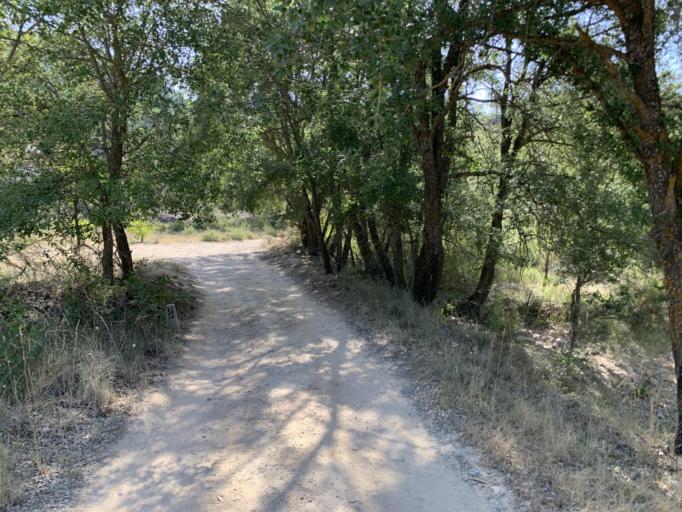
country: ES
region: Castille-La Mancha
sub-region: Provincia de Guadalajara
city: Ocentejo
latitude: 40.7645
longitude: -2.3919
